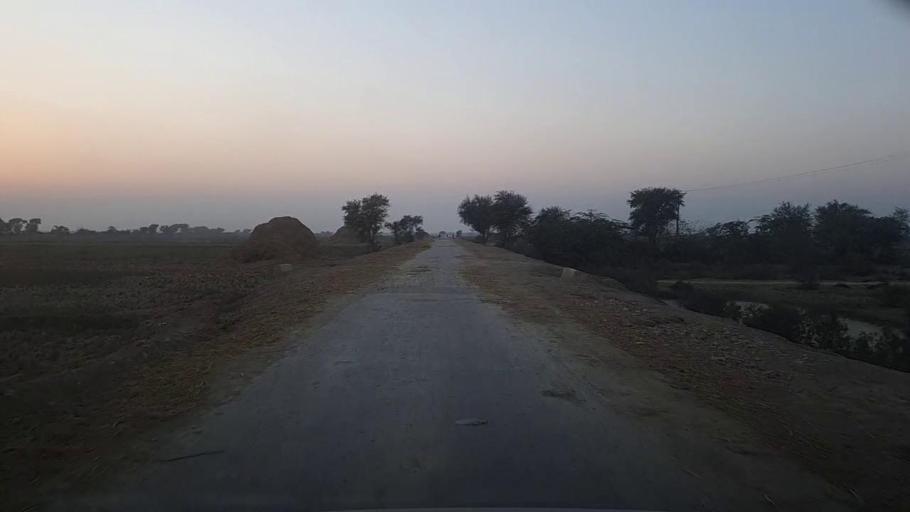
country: PK
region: Sindh
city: Khairpur Nathan Shah
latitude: 27.1783
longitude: 67.6247
